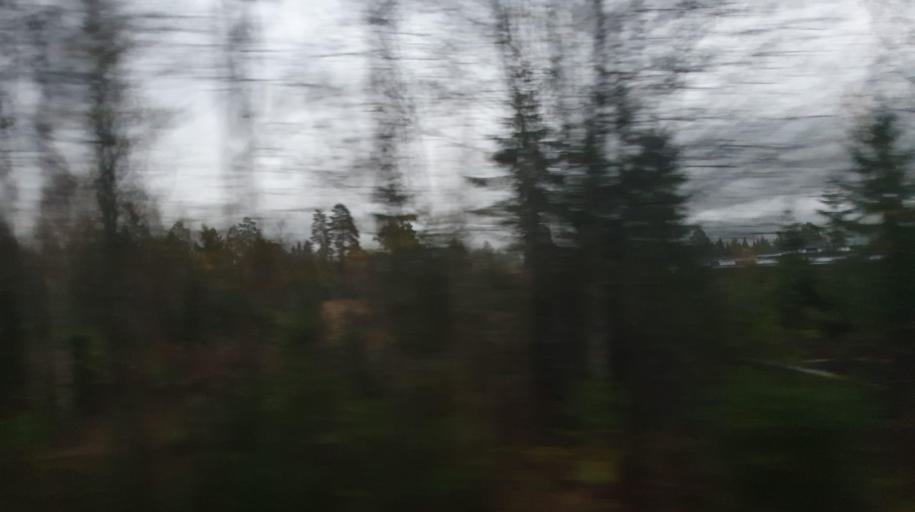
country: NO
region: Buskerud
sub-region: Krodsherad
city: Noresund
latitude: 60.1878
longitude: 9.5959
